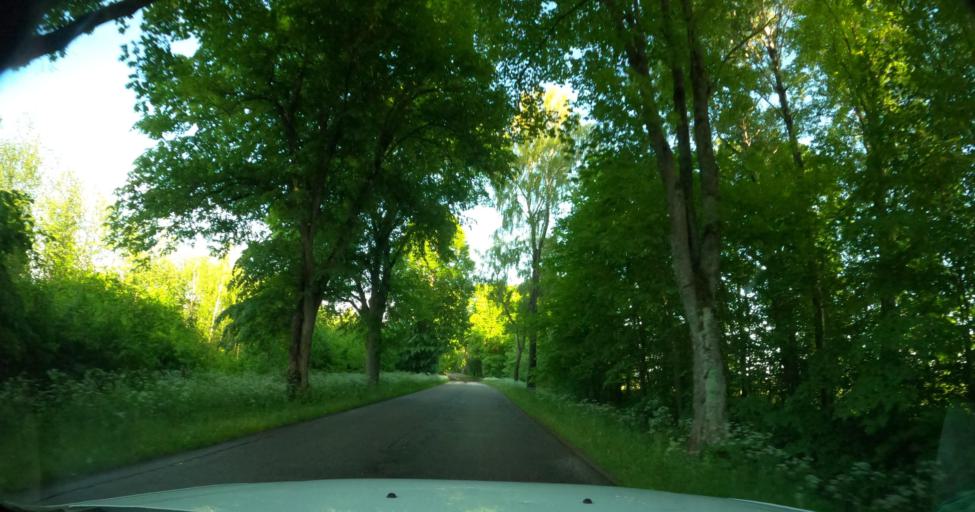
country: PL
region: Warmian-Masurian Voivodeship
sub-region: Powiat braniewski
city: Pieniezno
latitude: 54.2533
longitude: 20.0016
